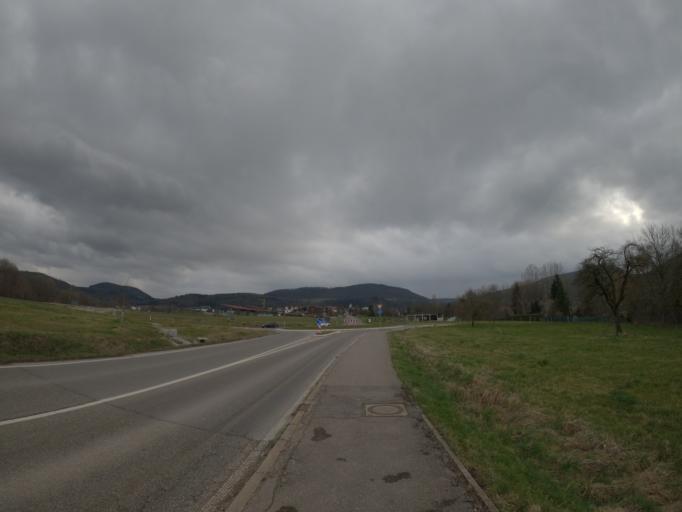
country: DE
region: Baden-Wuerttemberg
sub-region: Regierungsbezirk Stuttgart
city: Schlat
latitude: 48.6593
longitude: 9.7048
